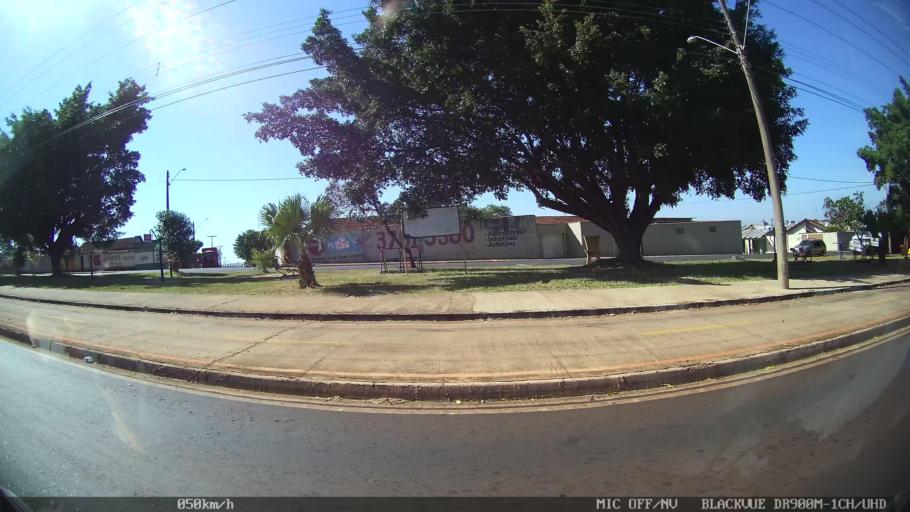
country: BR
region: Sao Paulo
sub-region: Batatais
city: Batatais
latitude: -20.9050
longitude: -47.5820
